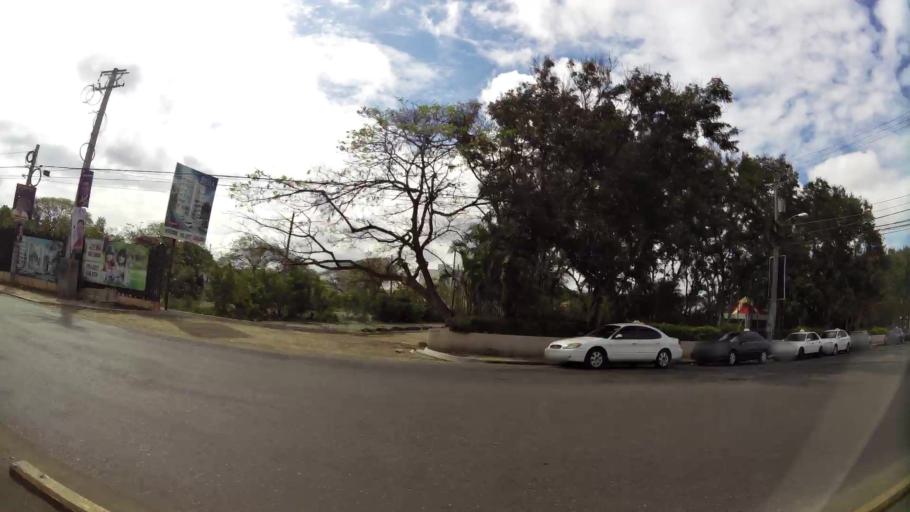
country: DO
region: Santiago
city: Santiago de los Caballeros
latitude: 19.4634
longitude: -70.6737
